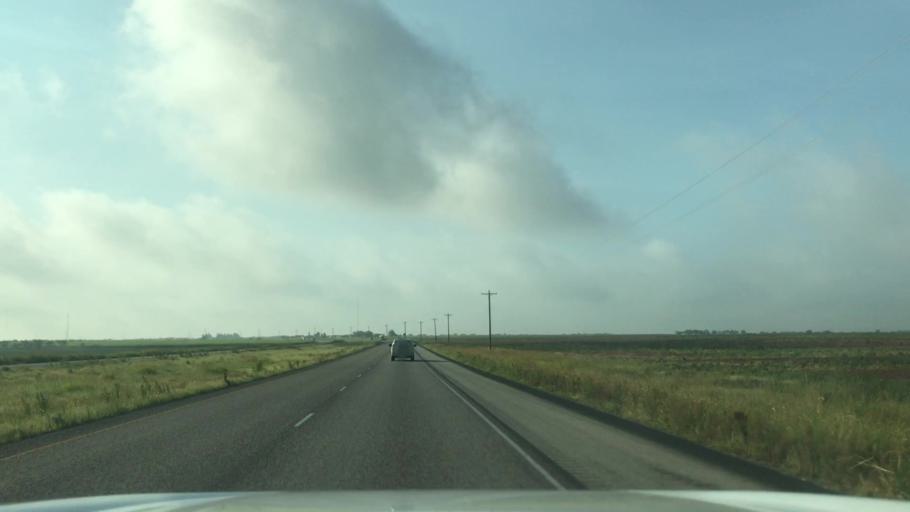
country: US
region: Texas
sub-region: Garza County
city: Post
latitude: 33.2235
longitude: -101.4401
